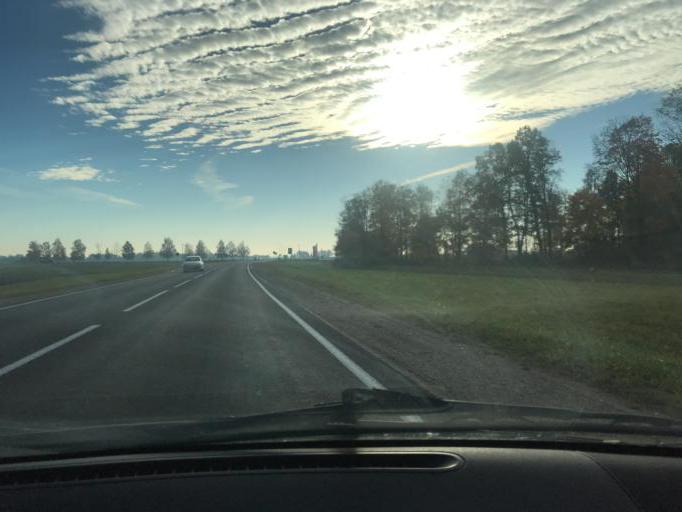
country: BY
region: Brest
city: Drahichyn
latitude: 52.2092
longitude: 25.2139
